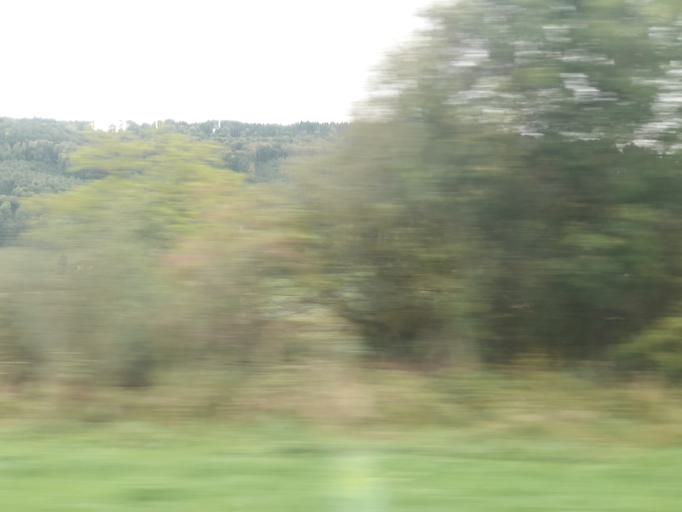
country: CH
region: Bern
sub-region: Bern-Mittelland District
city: Toffen
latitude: 46.8649
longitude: 7.4958
